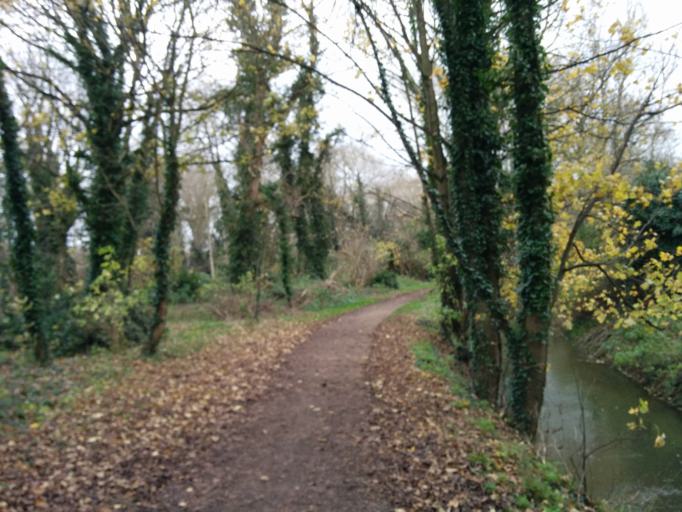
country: GB
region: England
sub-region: Oxfordshire
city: Abingdon
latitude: 51.6680
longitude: -1.2928
